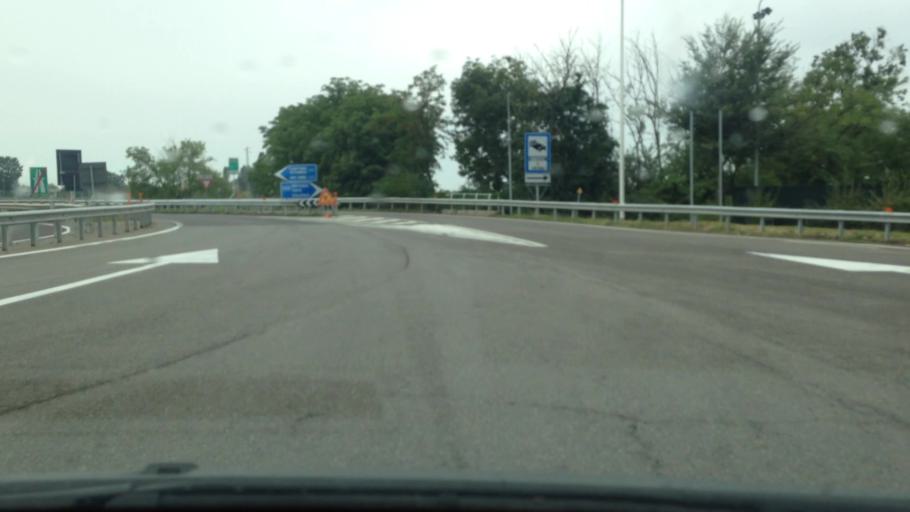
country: IT
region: Piedmont
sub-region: Provincia di Alessandria
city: Tortona
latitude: 44.9096
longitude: 8.8380
